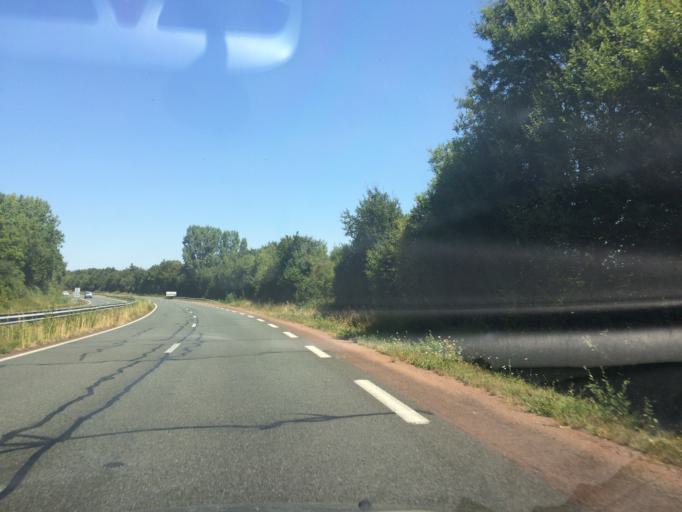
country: FR
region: Pays de la Loire
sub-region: Departement de la Vendee
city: Saint-Denis-la-Chevasse
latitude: 46.8702
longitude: -1.3975
